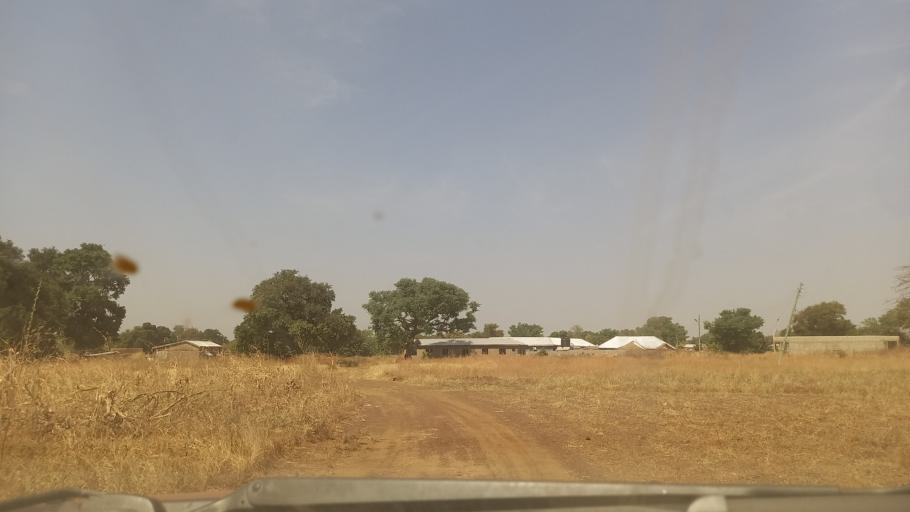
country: GH
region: Upper East
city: Navrongo
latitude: 10.8597
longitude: -1.0862
